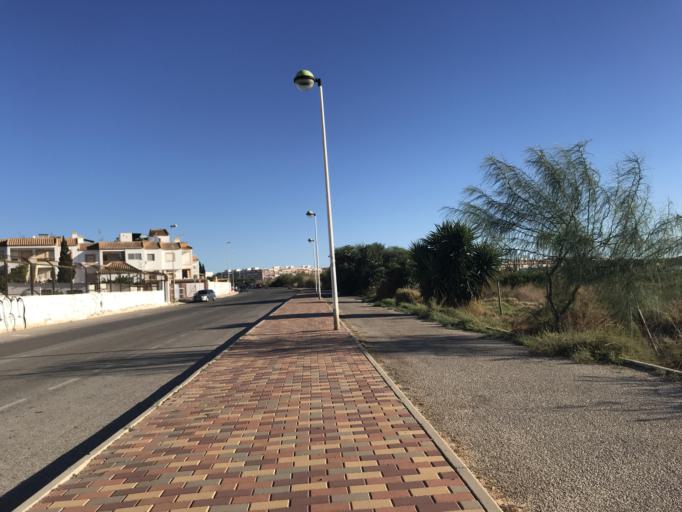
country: ES
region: Valencia
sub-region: Provincia de Alicante
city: Torrevieja
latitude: 37.9828
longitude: -0.6966
